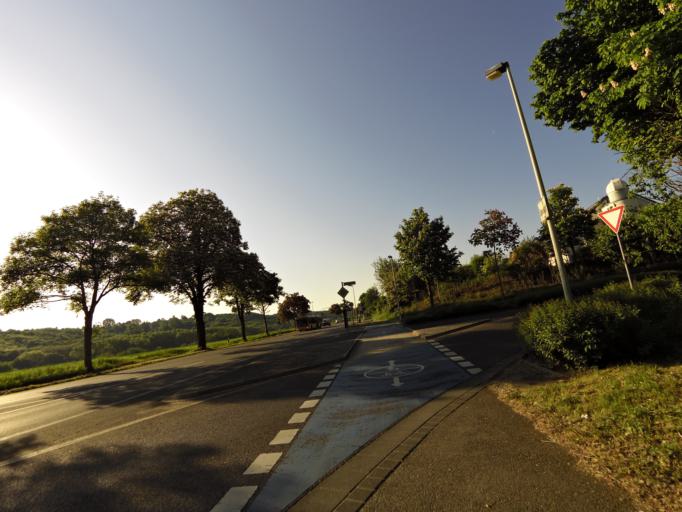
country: DE
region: North Rhine-Westphalia
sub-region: Regierungsbezirk Koln
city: Bonn
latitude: 50.6979
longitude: 7.0696
